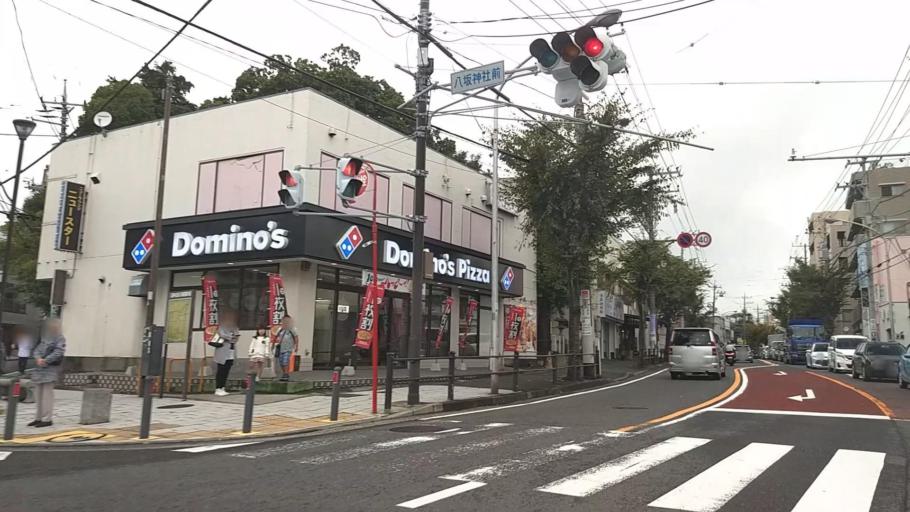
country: JP
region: Kanagawa
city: Fujisawa
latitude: 35.3949
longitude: 139.5299
